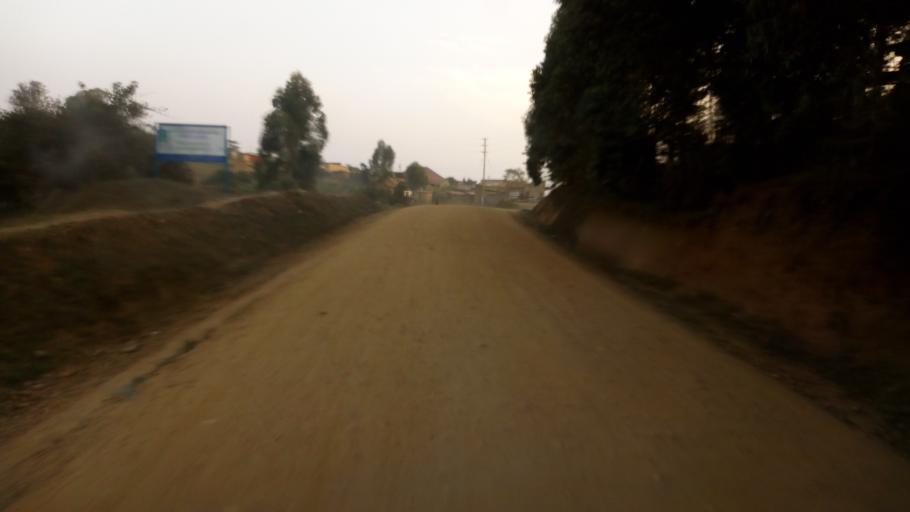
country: UG
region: Western Region
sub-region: Rukungiri District
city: Rukungiri
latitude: -0.7778
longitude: 29.9243
